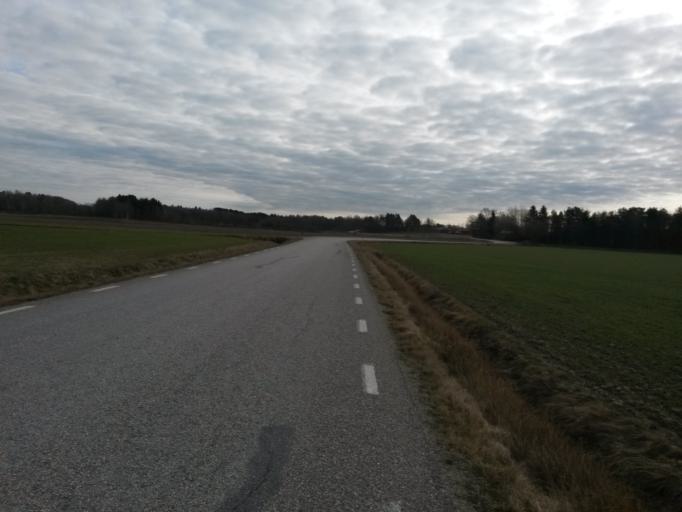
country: SE
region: Vaestra Goetaland
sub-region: Herrljunga Kommun
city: Herrljunga
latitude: 58.0883
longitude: 12.9127
